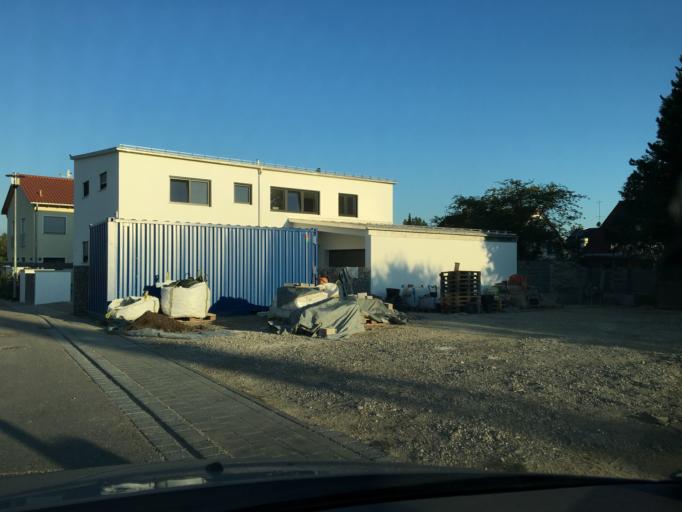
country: DE
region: Bavaria
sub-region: Upper Bavaria
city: Haimhausen
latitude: 48.3120
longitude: 11.5604
